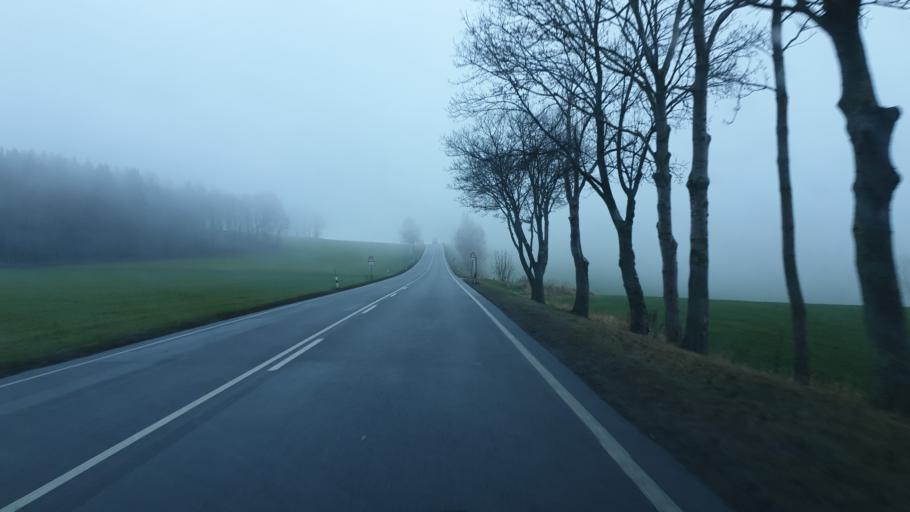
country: DE
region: Saxony
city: Grossolbersdorf
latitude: 50.6982
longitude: 13.1108
